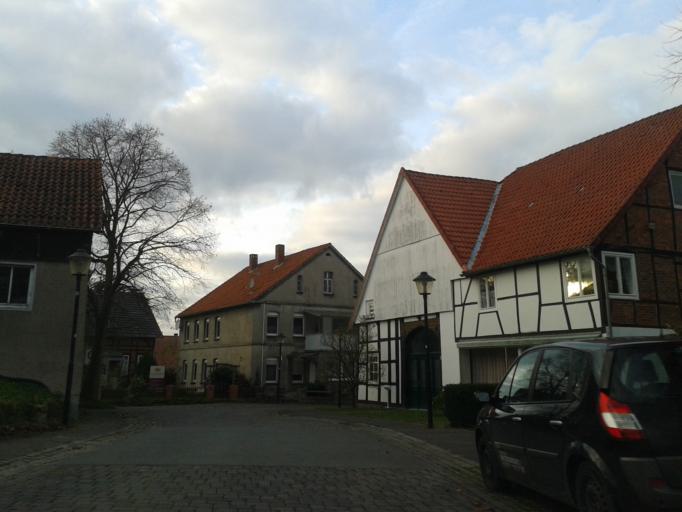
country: DE
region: North Rhine-Westphalia
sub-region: Regierungsbezirk Detmold
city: Bad Meinberg
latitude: 51.9140
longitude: 9.0286
